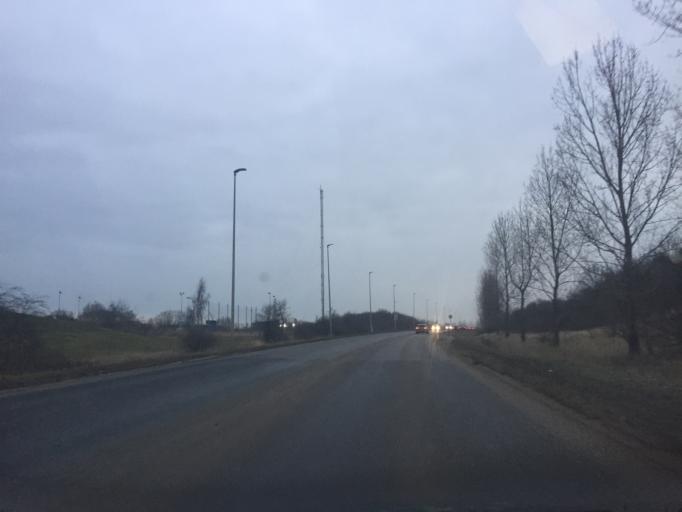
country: DK
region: Zealand
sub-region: Koge Kommune
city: Koge
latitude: 55.4709
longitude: 12.1892
